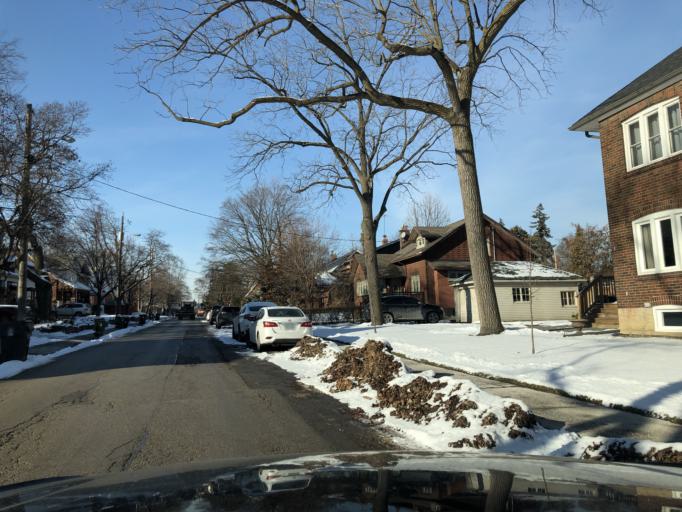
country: CA
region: Ontario
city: Etobicoke
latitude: 43.7051
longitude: -79.5187
